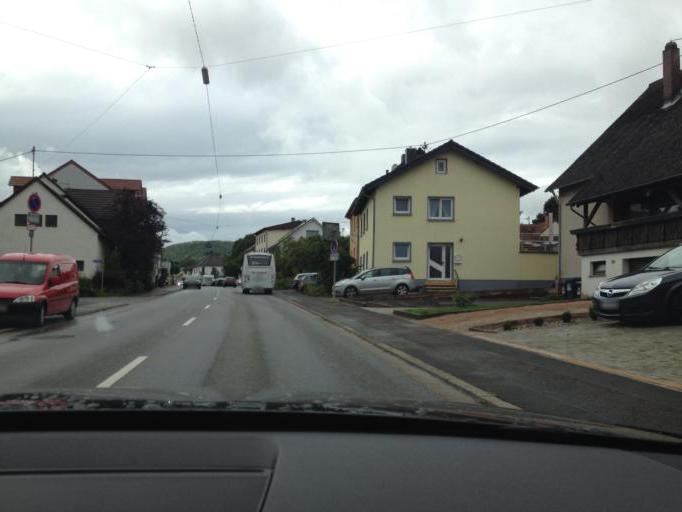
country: DE
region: Saarland
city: Oberthal
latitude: 49.5088
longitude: 7.0906
